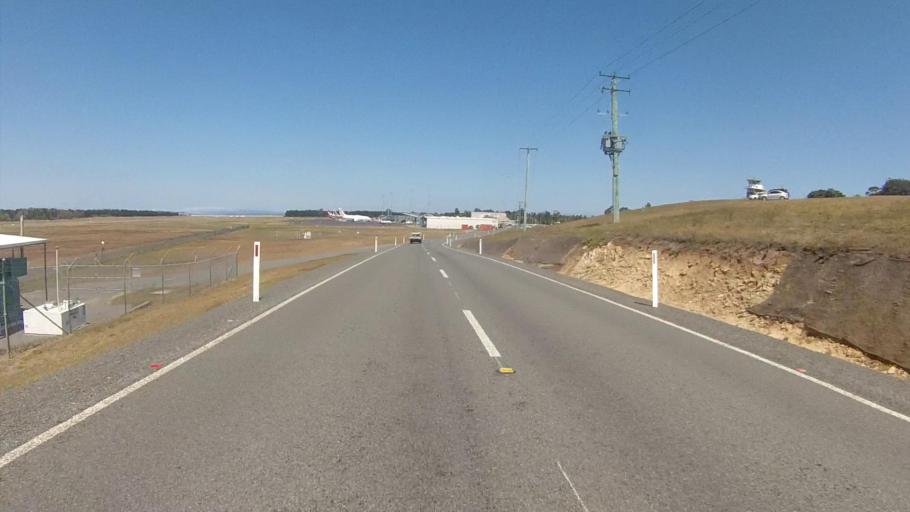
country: AU
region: Tasmania
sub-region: Clarence
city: Seven Mile Beach
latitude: -42.8328
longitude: 147.5016
